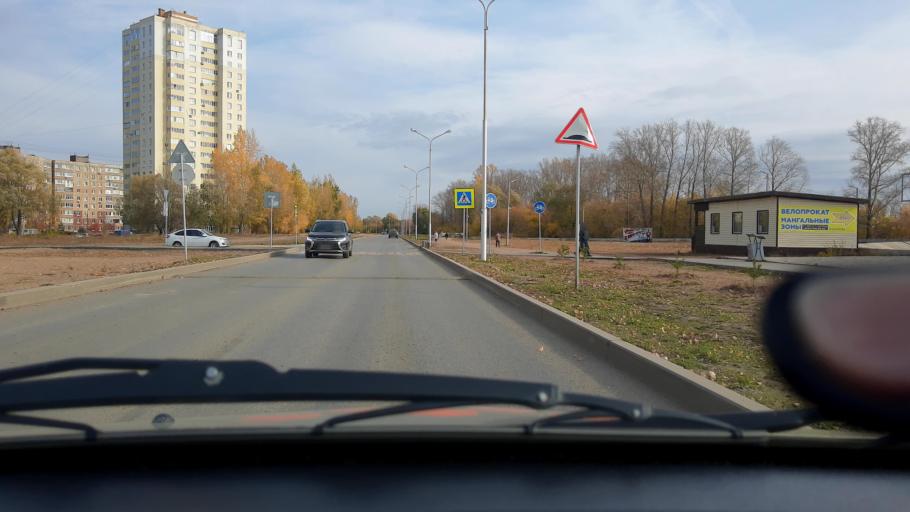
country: RU
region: Bashkortostan
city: Ufa
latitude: 54.7636
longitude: 56.0758
